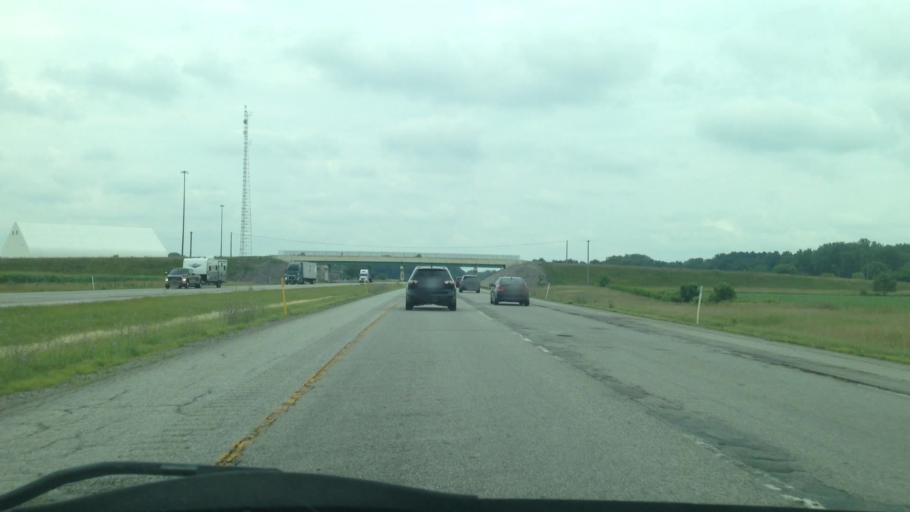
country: US
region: Michigan
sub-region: Saint Joseph County
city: White Pigeon
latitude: 41.7460
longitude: -85.5402
